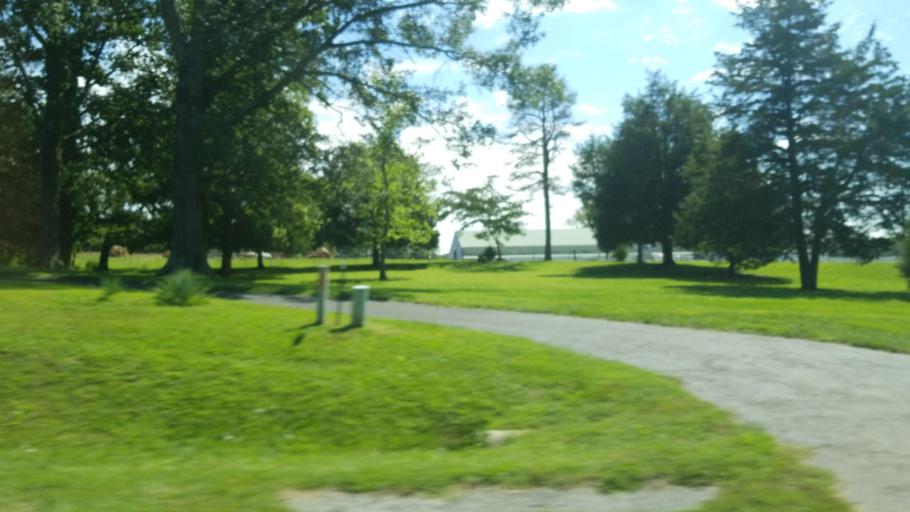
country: US
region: Illinois
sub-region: Williamson County
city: Johnston City
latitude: 37.7892
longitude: -88.9109
